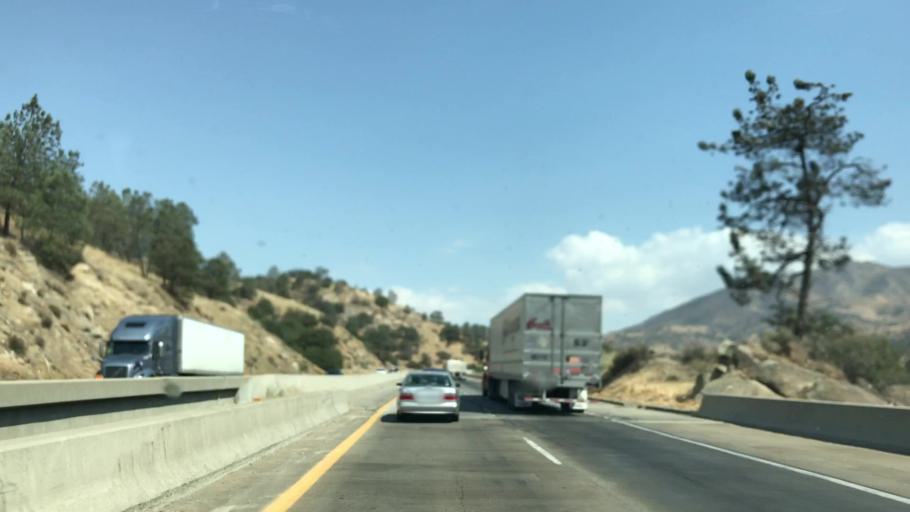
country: US
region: California
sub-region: Kern County
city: Bear Valley Springs
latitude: 35.2214
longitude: -118.5563
